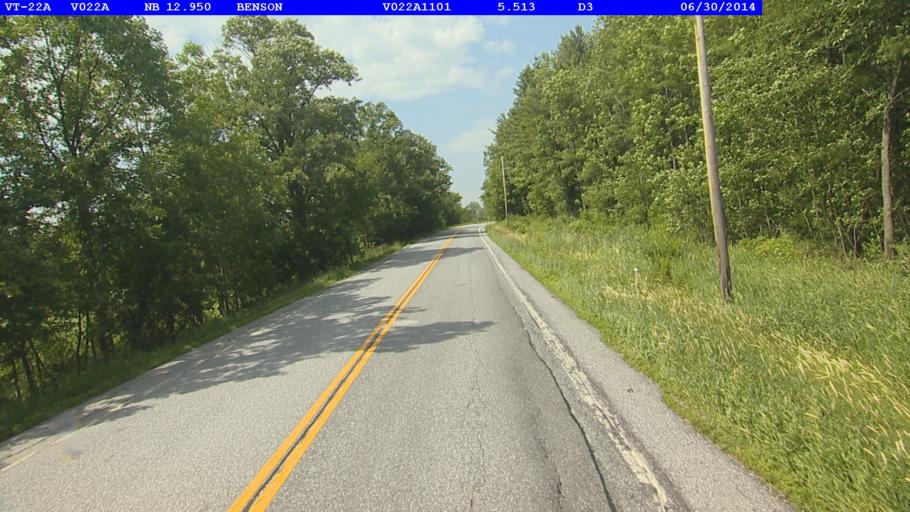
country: US
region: New York
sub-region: Essex County
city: Ticonderoga
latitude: 43.7469
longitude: -73.3077
